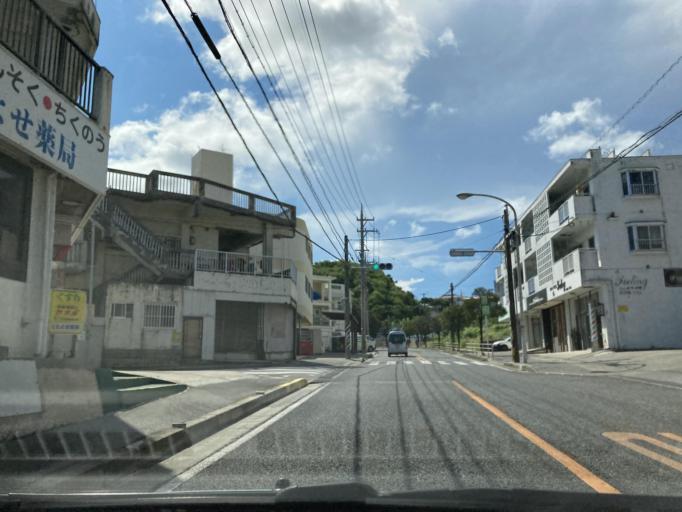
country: JP
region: Okinawa
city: Tomigusuku
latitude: 26.1741
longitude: 127.7193
